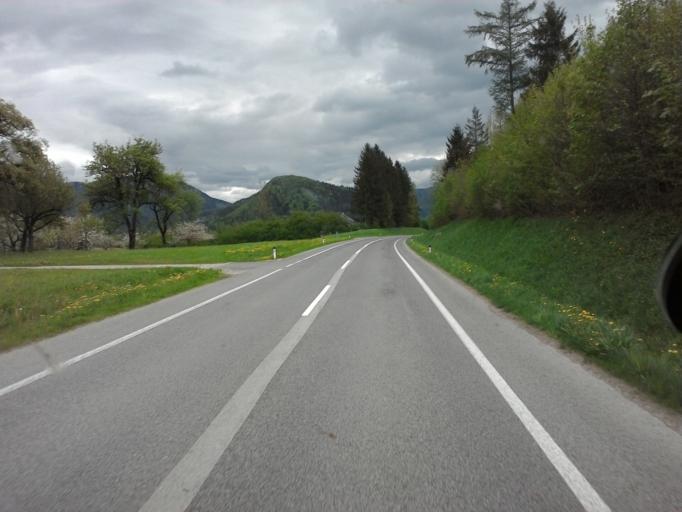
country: AT
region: Upper Austria
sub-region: Politischer Bezirk Kirchdorf an der Krems
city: Rossleithen
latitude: 47.7335
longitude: 14.2855
